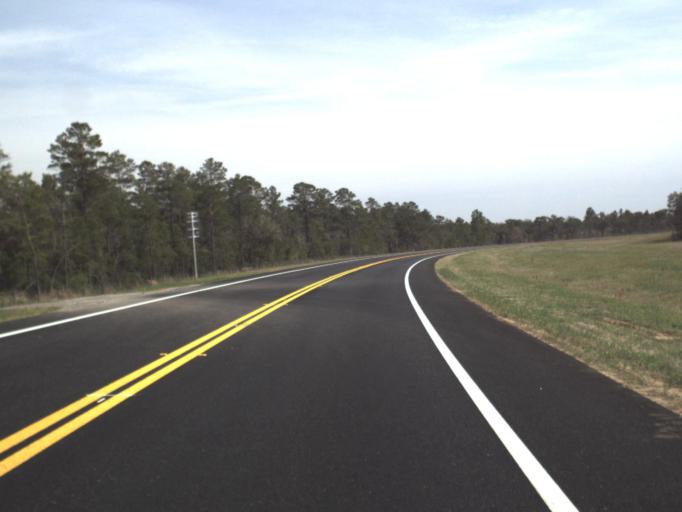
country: US
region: Florida
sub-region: Okaloosa County
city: Niceville
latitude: 30.5335
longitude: -86.4213
